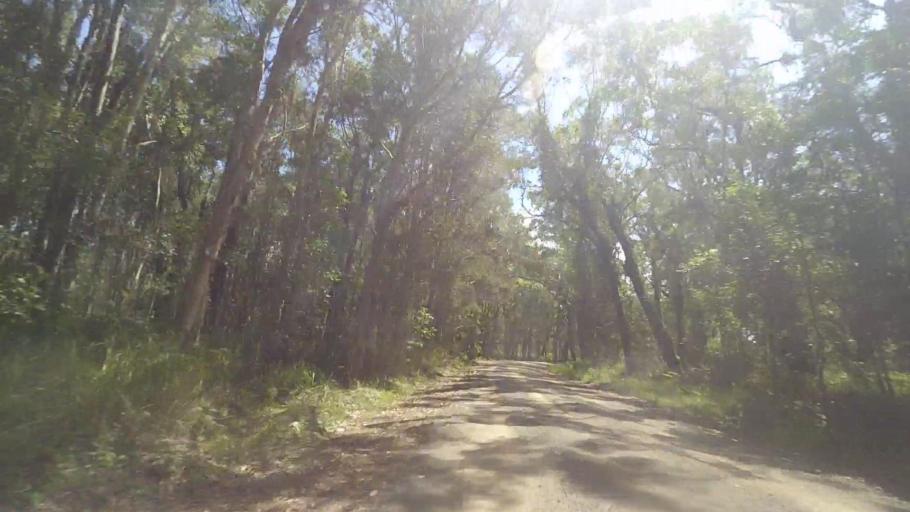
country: AU
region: New South Wales
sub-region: Great Lakes
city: Bulahdelah
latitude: -32.5097
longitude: 152.2934
